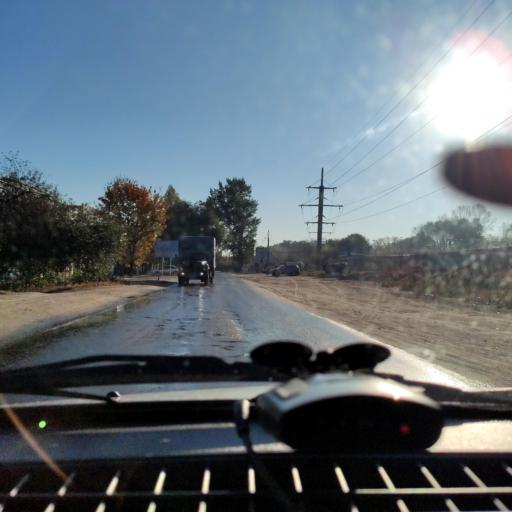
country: RU
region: Voronezj
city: Voronezh
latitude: 51.6680
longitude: 39.1462
